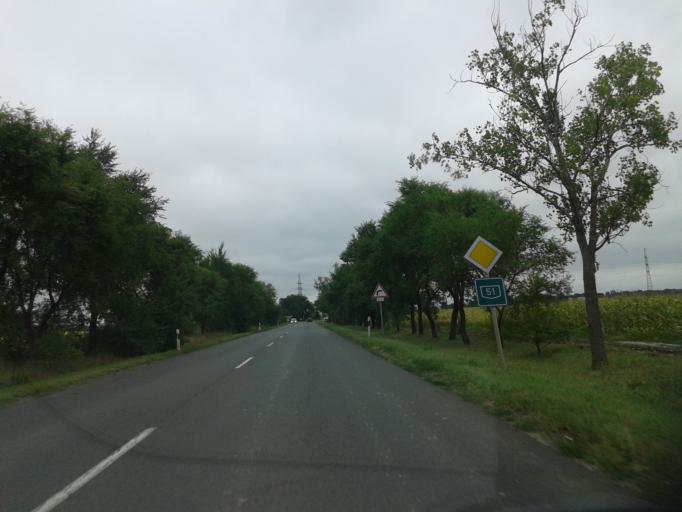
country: HU
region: Bacs-Kiskun
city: Solt
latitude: 46.8462
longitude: 19.0009
